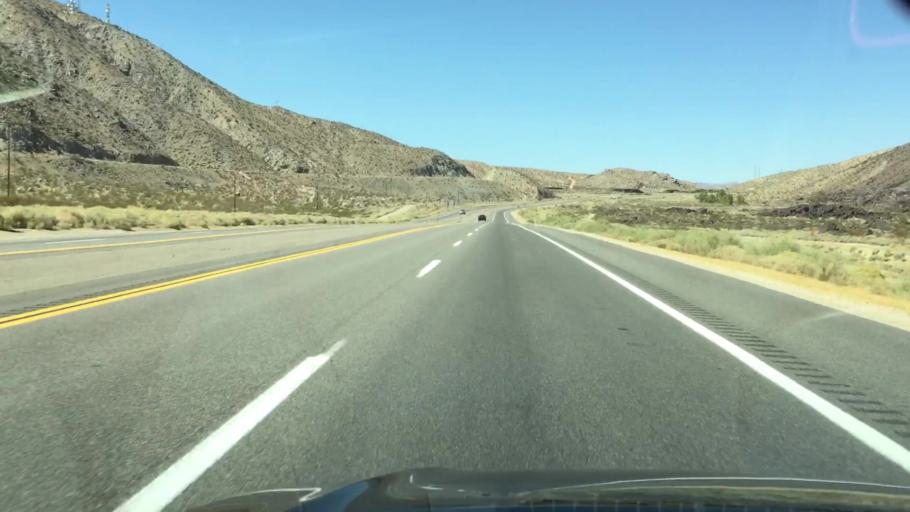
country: US
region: California
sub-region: Kern County
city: Inyokern
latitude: 35.9189
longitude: -117.9063
